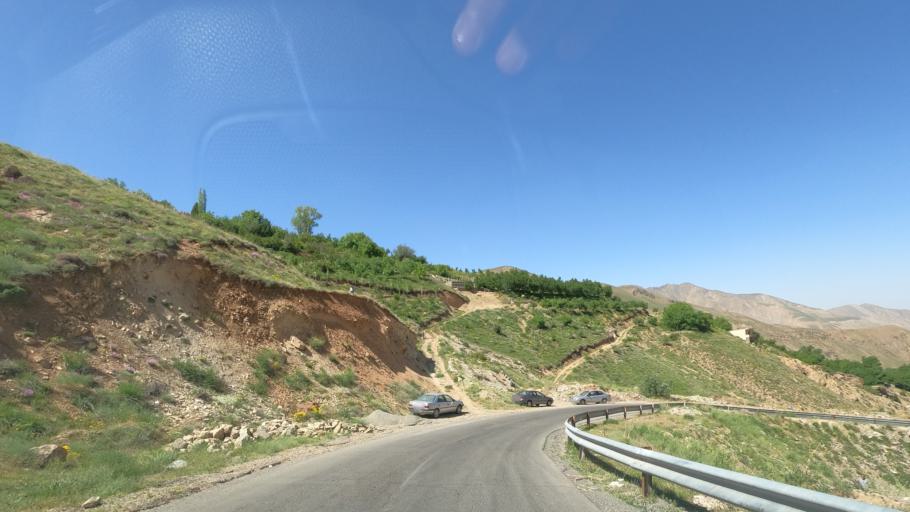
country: IR
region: Alborz
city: Karaj
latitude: 35.9226
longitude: 51.1580
